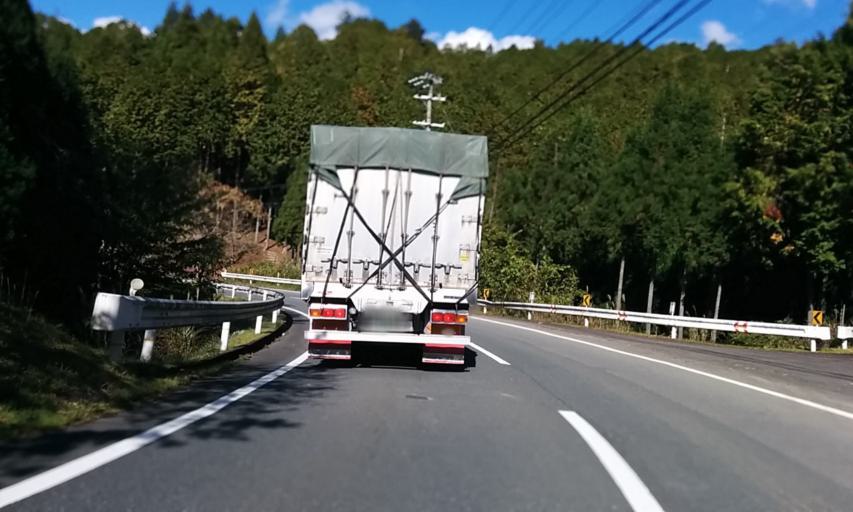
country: JP
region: Kyoto
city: Kameoka
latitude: 35.2040
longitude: 135.6171
